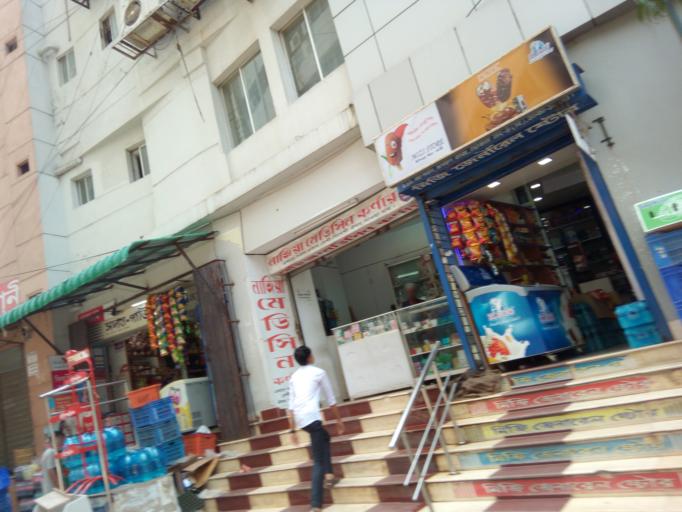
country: BD
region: Dhaka
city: Paltan
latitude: 23.7331
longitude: 90.4119
